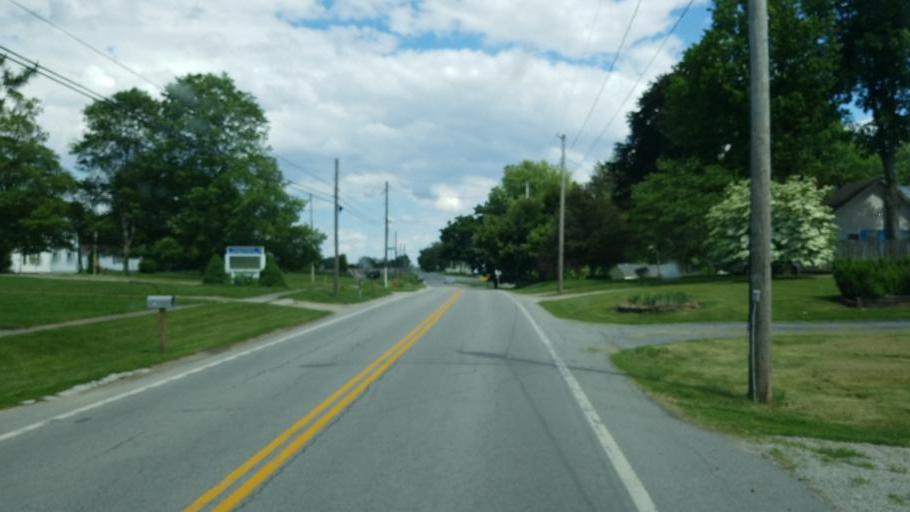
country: US
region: Ohio
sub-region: Huron County
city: Greenwich
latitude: 41.1041
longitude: -82.6089
